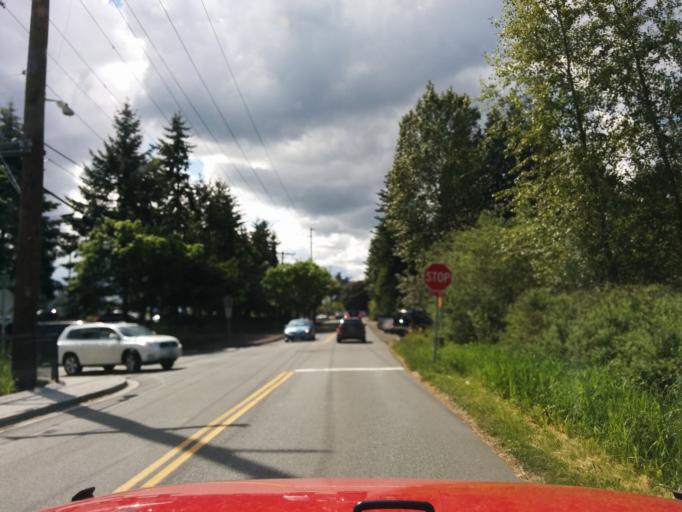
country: US
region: Washington
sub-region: King County
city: Kirkland
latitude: 47.6825
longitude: -122.1803
